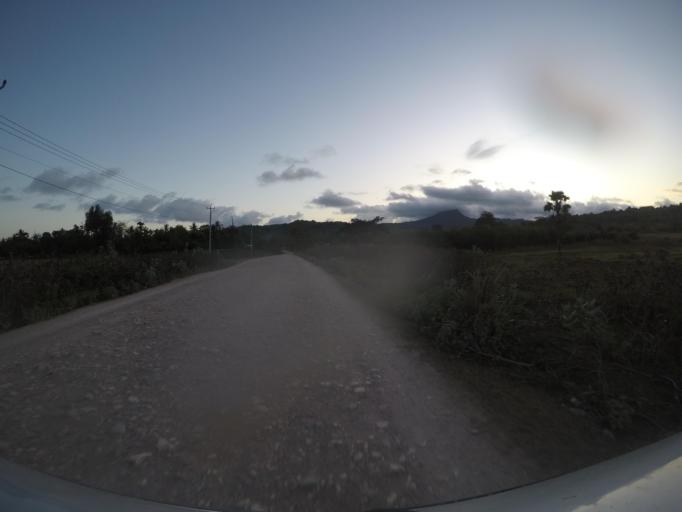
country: TL
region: Viqueque
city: Viqueque
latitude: -8.7716
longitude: 126.6408
